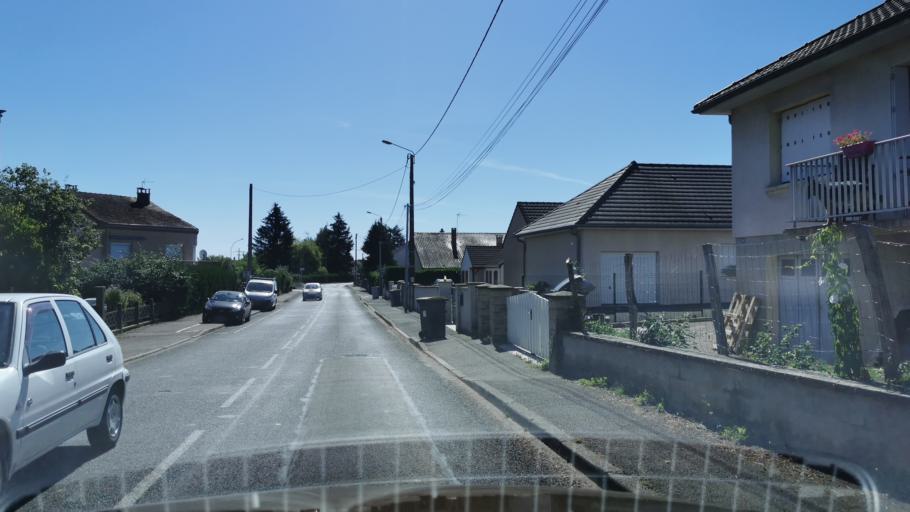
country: FR
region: Bourgogne
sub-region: Departement de Saone-et-Loire
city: Le Breuil
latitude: 46.8020
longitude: 4.4734
